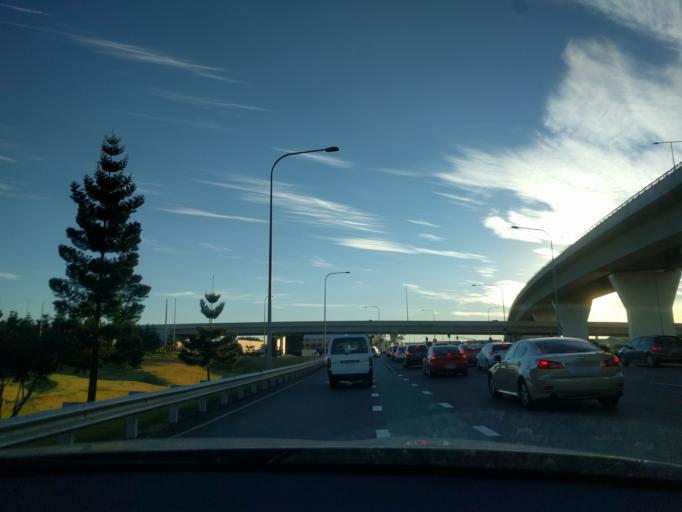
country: AU
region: Queensland
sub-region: Brisbane
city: Ascot
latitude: -27.4125
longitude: 153.0787
